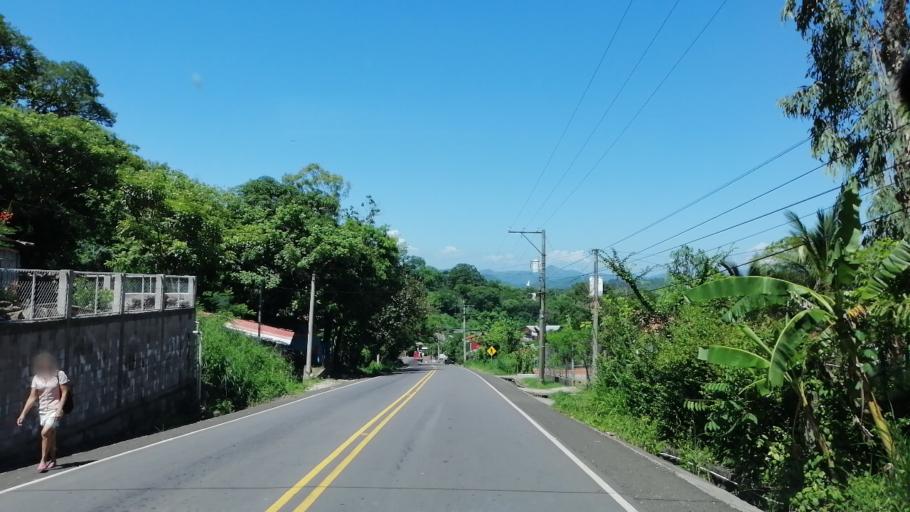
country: SV
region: Morazan
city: Cacaopera
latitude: 13.8071
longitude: -88.1478
